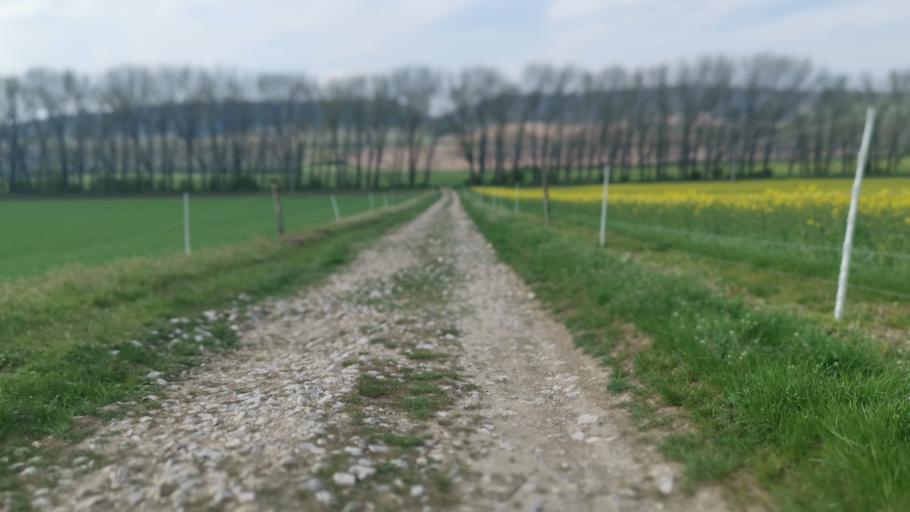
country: SK
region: Trnavsky
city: Smolenice
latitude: 48.5345
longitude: 17.3803
